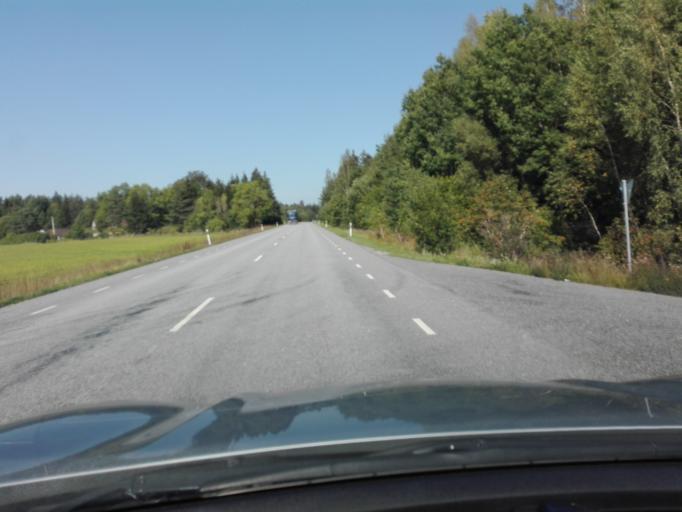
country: EE
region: Raplamaa
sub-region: Rapla vald
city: Rapla
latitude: 59.0014
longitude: 24.7689
